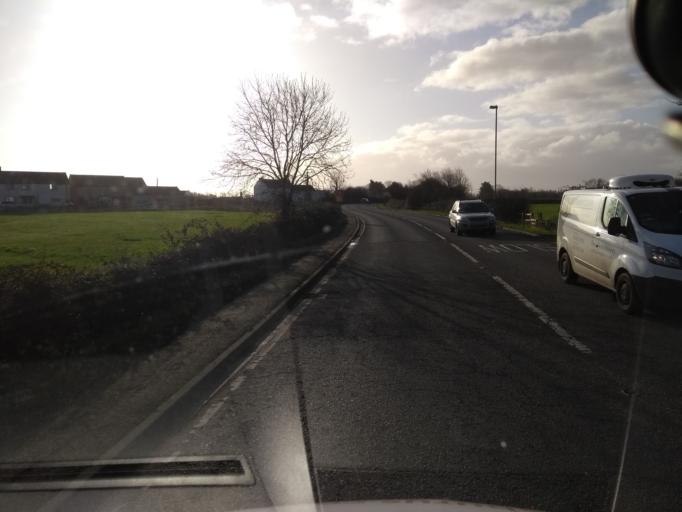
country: GB
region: England
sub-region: North Somerset
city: Bleadon
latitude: 51.2628
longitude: -2.9346
